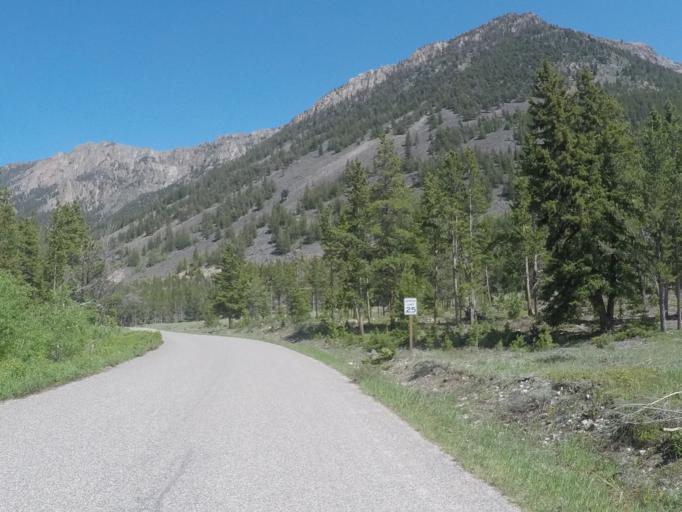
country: US
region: Montana
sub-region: Carbon County
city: Red Lodge
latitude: 45.0584
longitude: -109.4085
